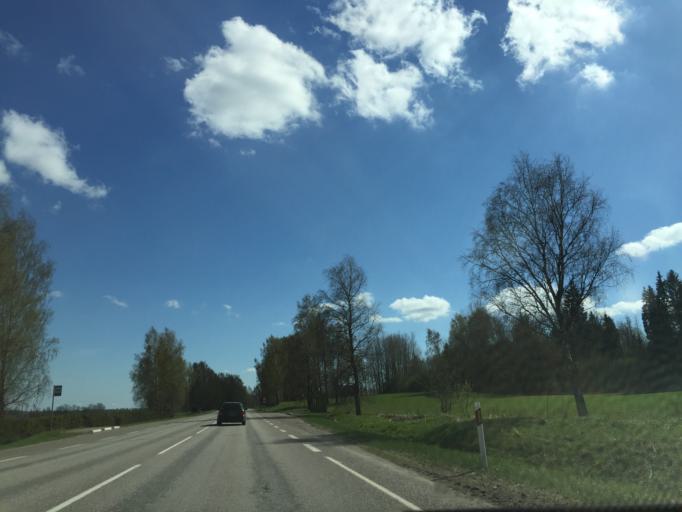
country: EE
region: Valgamaa
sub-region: Valga linn
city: Valga
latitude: 57.8898
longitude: 26.0562
